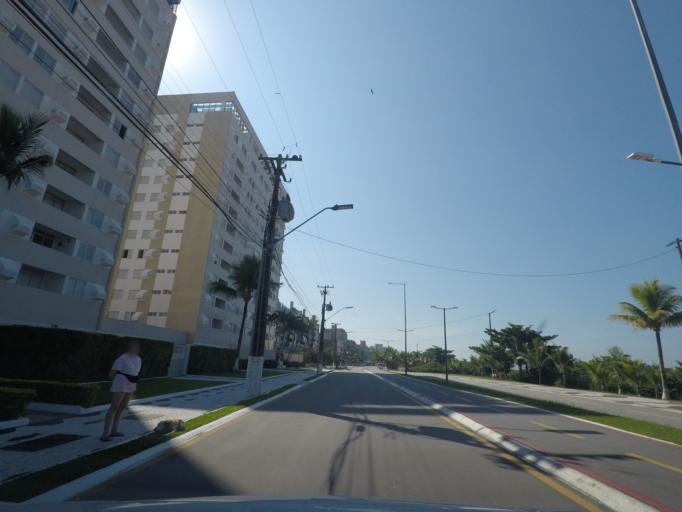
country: BR
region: Parana
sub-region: Guaratuba
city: Guaratuba
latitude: -25.8335
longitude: -48.5371
